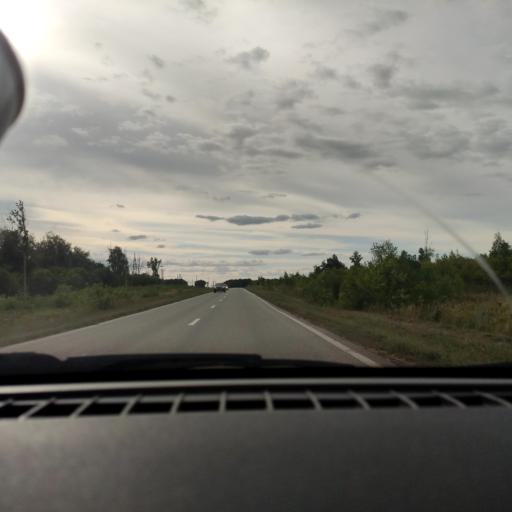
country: RU
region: Samara
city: Georgiyevka
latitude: 53.4262
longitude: 50.8136
